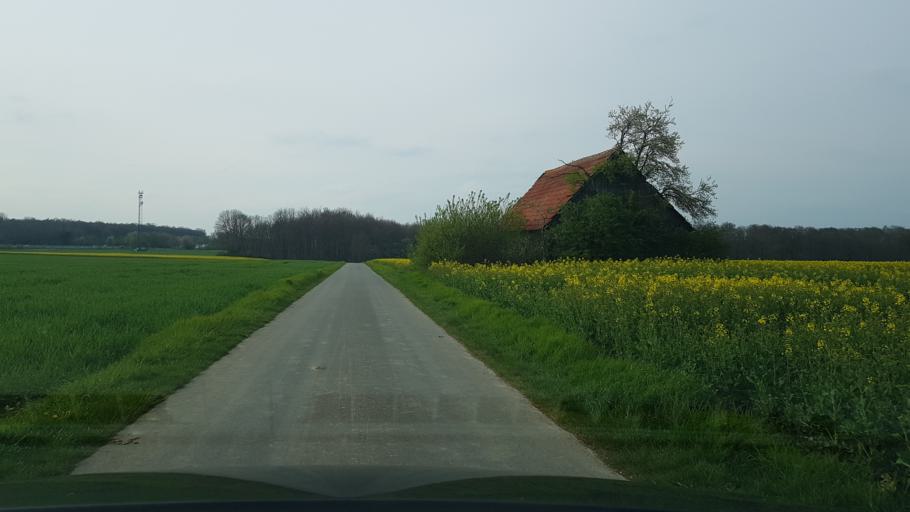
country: DE
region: North Rhine-Westphalia
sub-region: Regierungsbezirk Detmold
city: Paderborn
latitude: 51.6247
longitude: 8.7308
